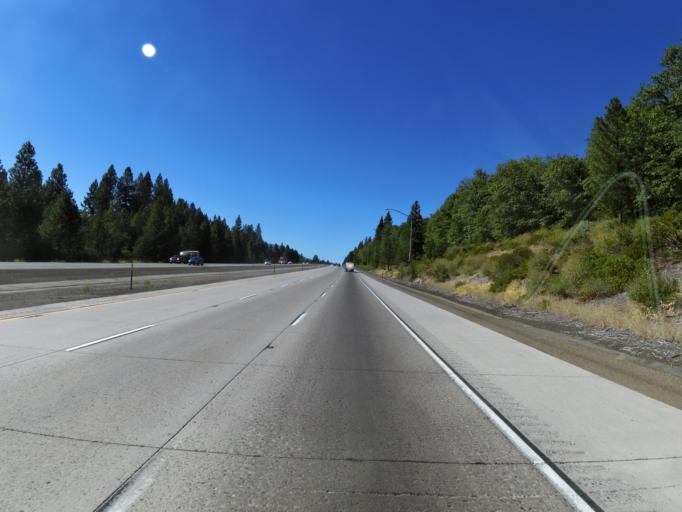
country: US
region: California
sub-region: Siskiyou County
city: Dunsmuir
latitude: 41.2517
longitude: -122.2604
